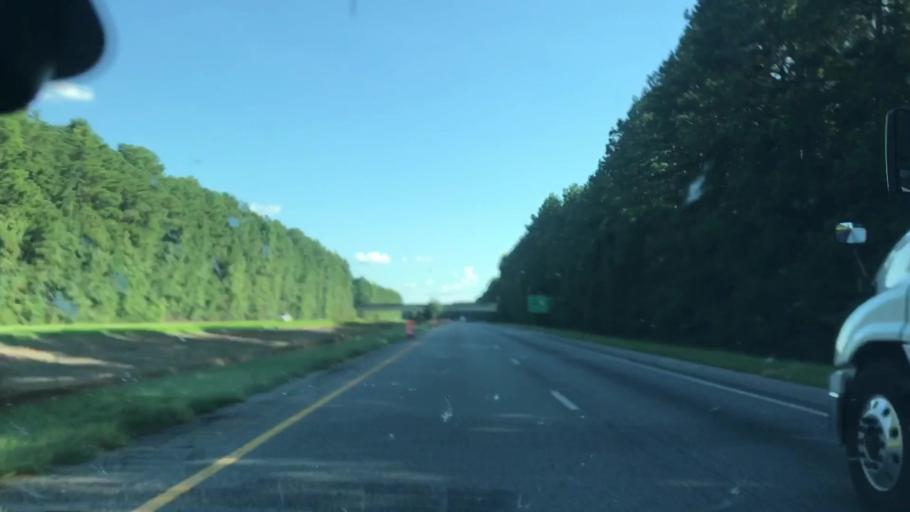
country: US
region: Georgia
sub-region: Harris County
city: Hamilton
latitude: 32.6825
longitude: -84.9902
